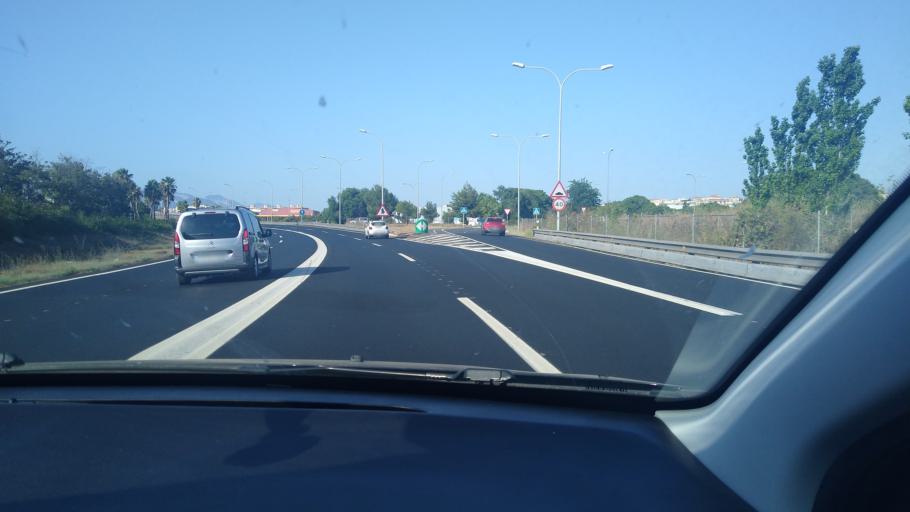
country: ES
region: Balearic Islands
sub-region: Illes Balears
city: Palma
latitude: 39.5885
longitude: 2.6703
